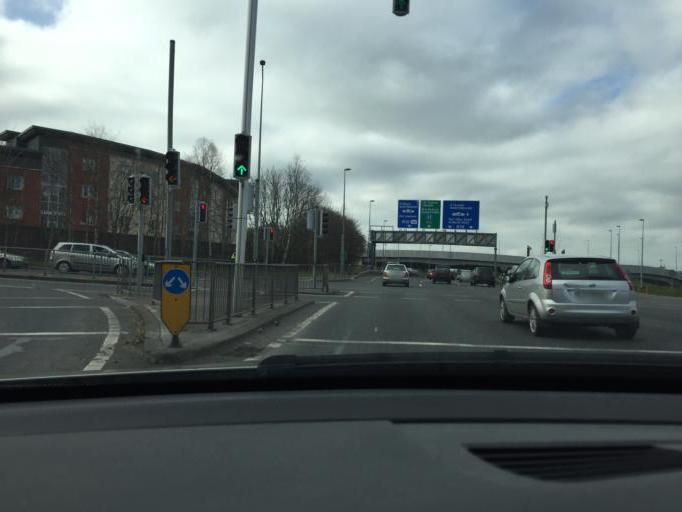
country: IE
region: Leinster
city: Castleknock
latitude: 53.3806
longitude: -6.3577
